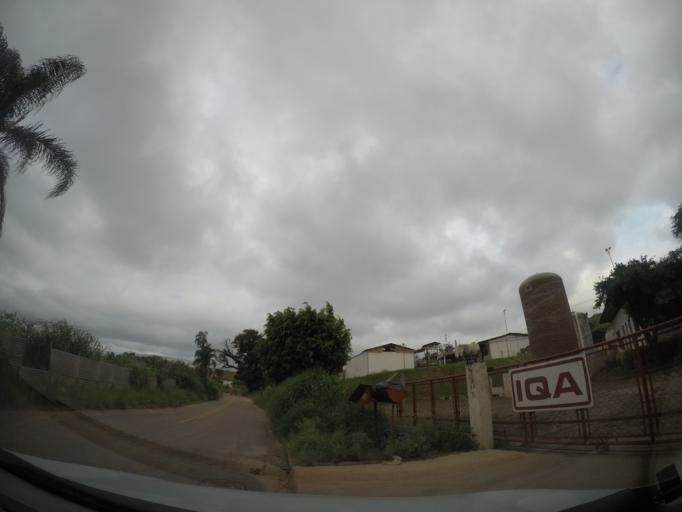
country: BR
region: Sao Paulo
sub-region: Aruja
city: Aruja
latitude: -23.4134
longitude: -46.3648
